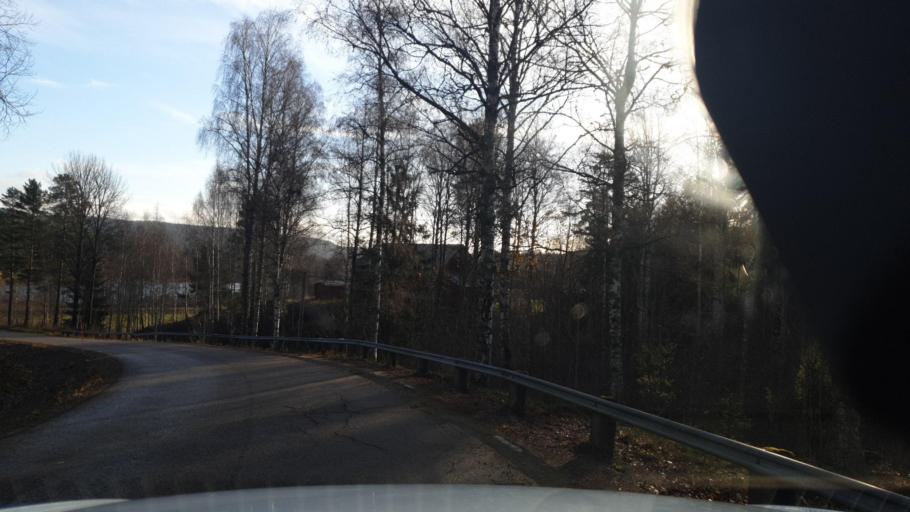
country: NO
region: Ostfold
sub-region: Romskog
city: Romskog
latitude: 59.8096
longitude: 12.0030
